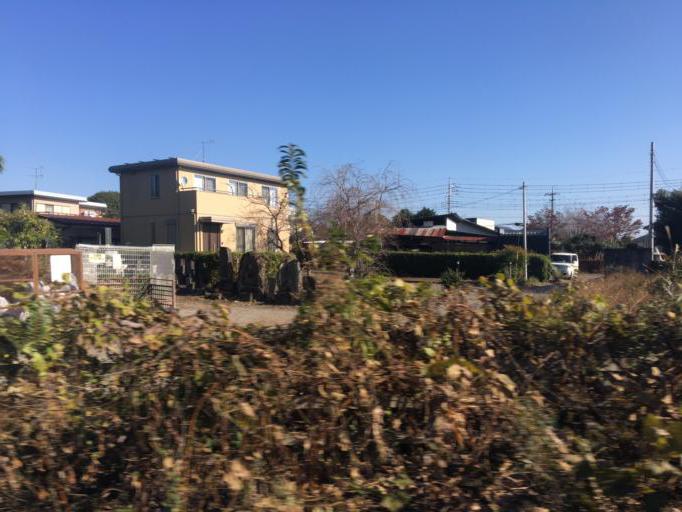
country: JP
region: Gunma
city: Isesaki
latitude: 36.3411
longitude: 139.1667
